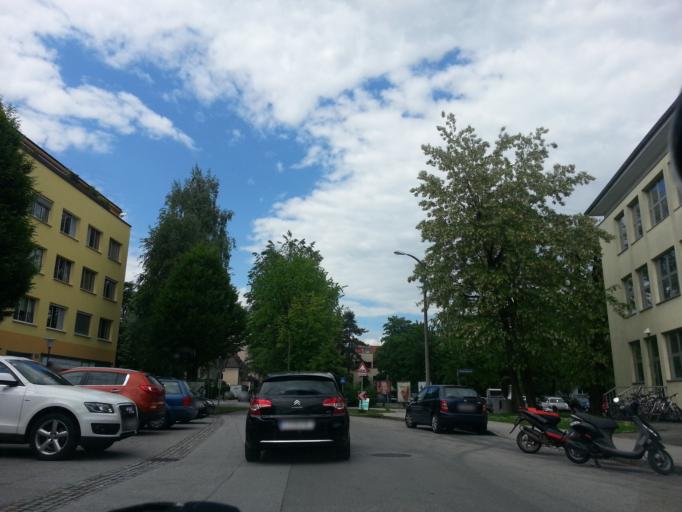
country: AT
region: Salzburg
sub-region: Salzburg Stadt
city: Salzburg
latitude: 47.8120
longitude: 13.0344
